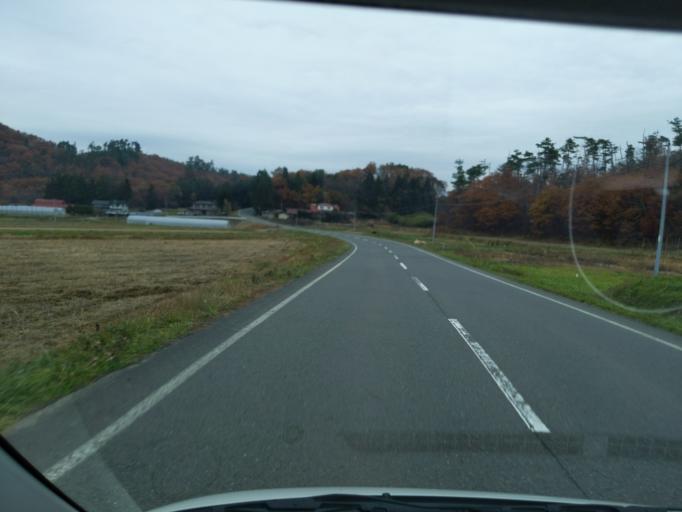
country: JP
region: Iwate
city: Kitakami
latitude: 39.2366
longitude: 141.2197
